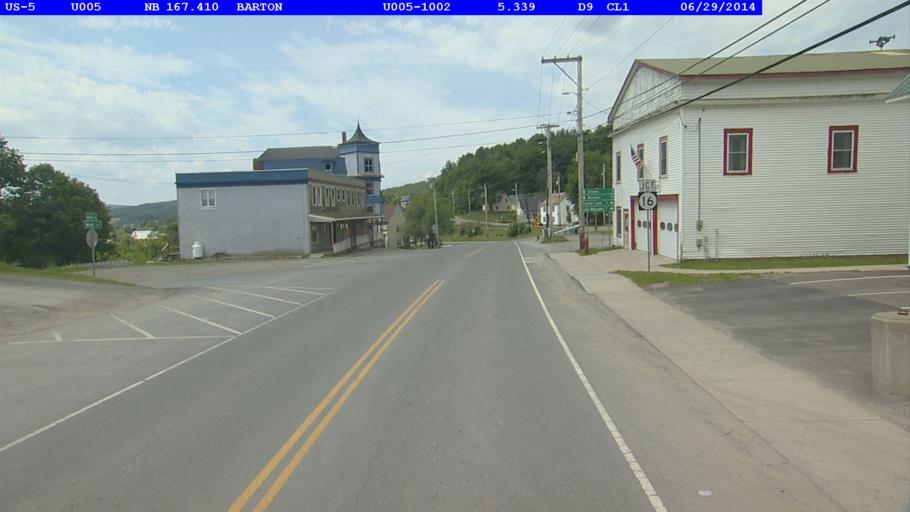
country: US
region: Vermont
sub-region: Orleans County
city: Newport
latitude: 44.7471
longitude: -72.1758
